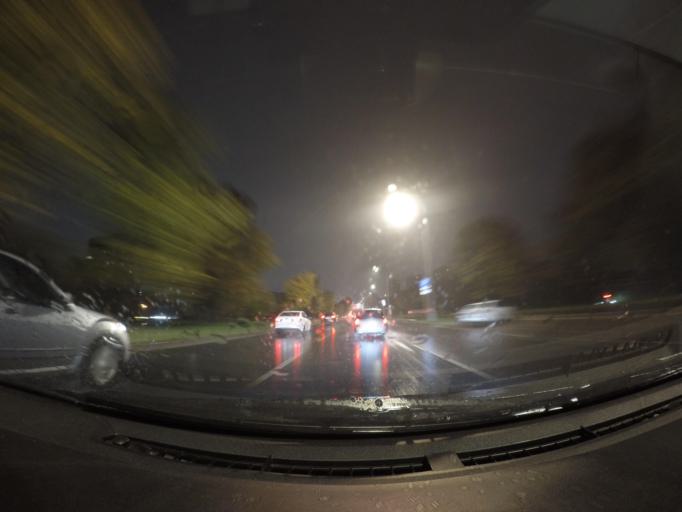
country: RU
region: Moscow
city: Kolomenskoye
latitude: 55.6713
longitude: 37.6627
